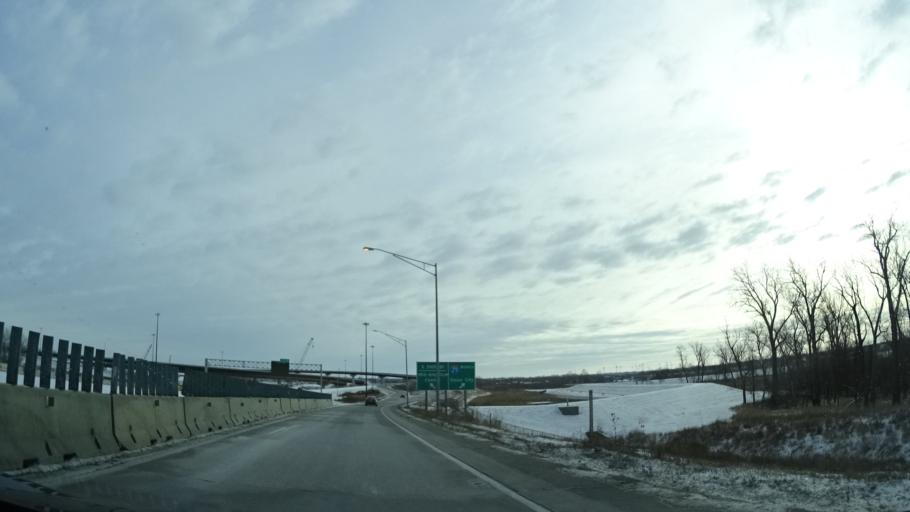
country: US
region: Nebraska
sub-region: Douglas County
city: Omaha
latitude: 41.2318
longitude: -95.9049
